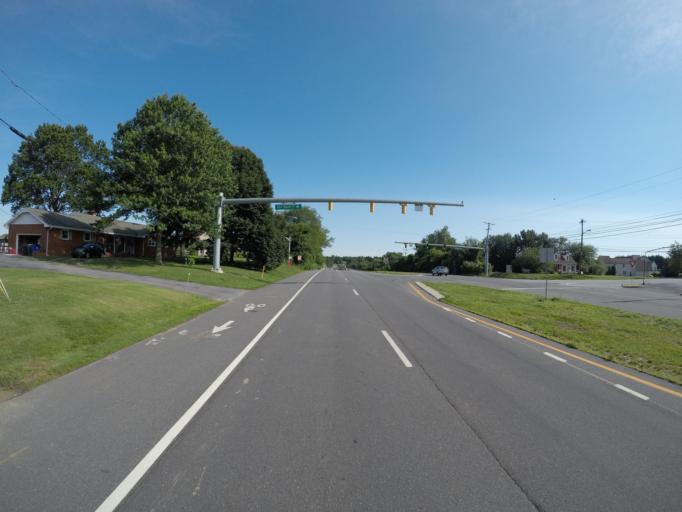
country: US
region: Delaware
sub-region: New Castle County
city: Bear
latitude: 39.5643
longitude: -75.6540
